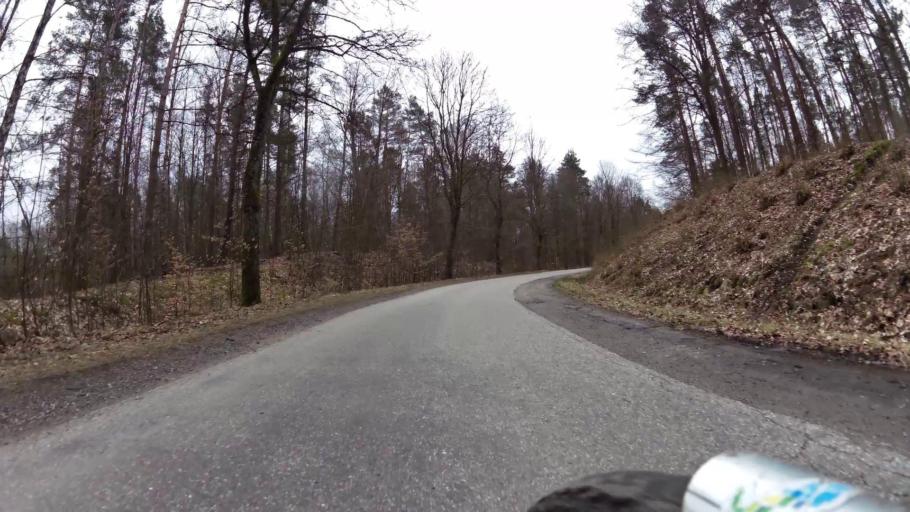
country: PL
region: Pomeranian Voivodeship
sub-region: Powiat bytowski
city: Trzebielino
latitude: 54.0976
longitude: 17.1340
